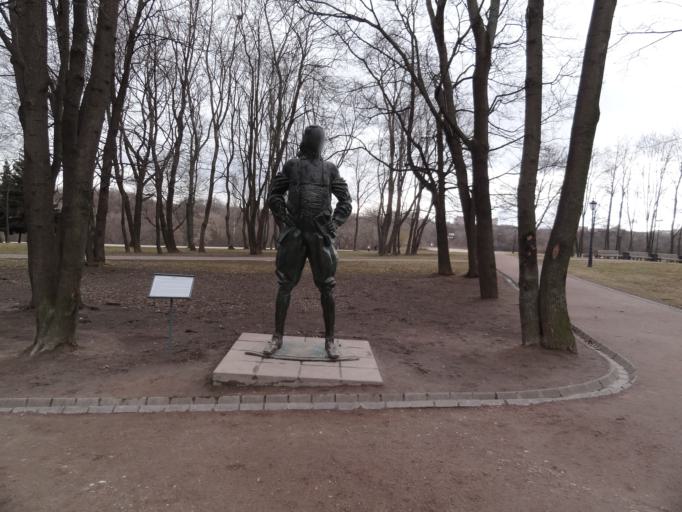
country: RU
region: Moscow
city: Kolomenskoye
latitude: 55.6673
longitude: 37.6670
